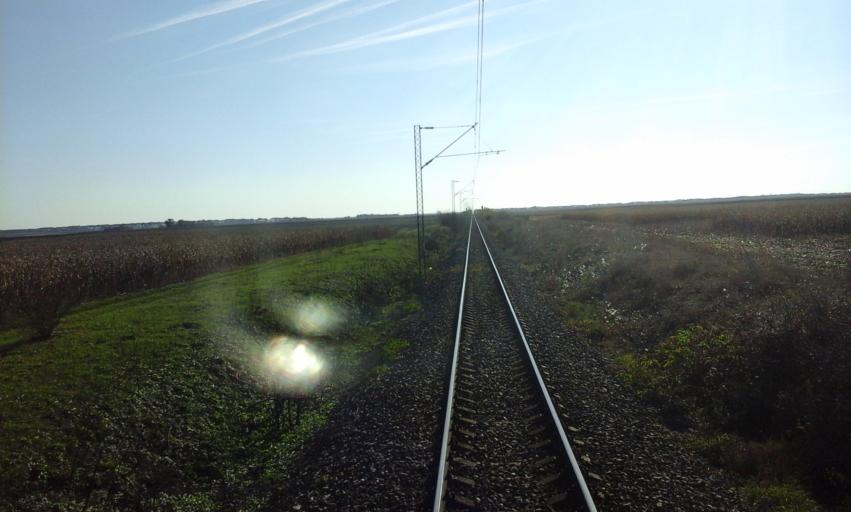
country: RS
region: Autonomna Pokrajina Vojvodina
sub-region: Severnobacki Okrug
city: Backa Topola
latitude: 45.9039
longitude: 19.6628
